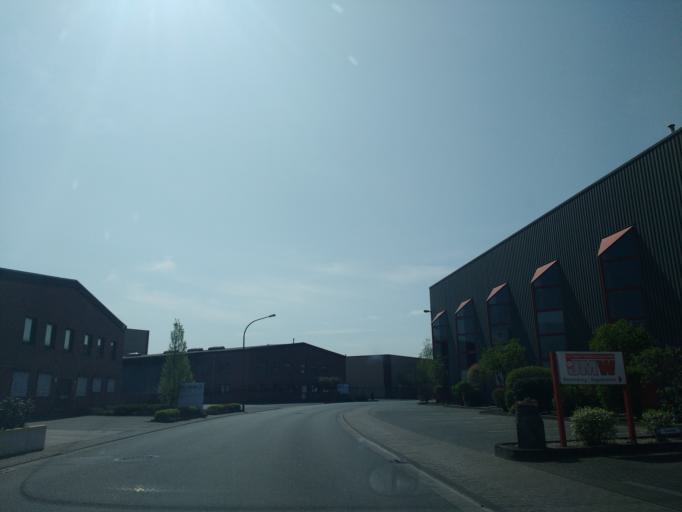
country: DE
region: North Rhine-Westphalia
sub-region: Regierungsbezirk Detmold
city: Hovelhof
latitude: 51.8340
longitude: 8.6493
